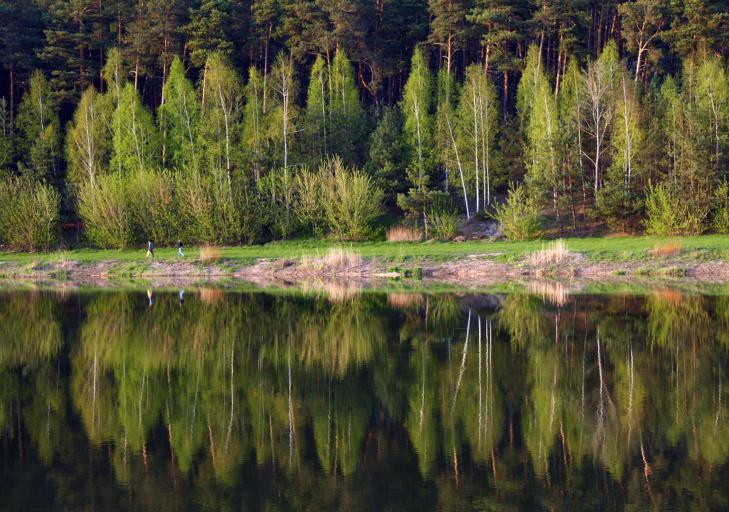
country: PL
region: Swietokrzyskie
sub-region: Powiat ostrowiecki
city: Cmielow
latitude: 50.9022
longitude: 21.5108
